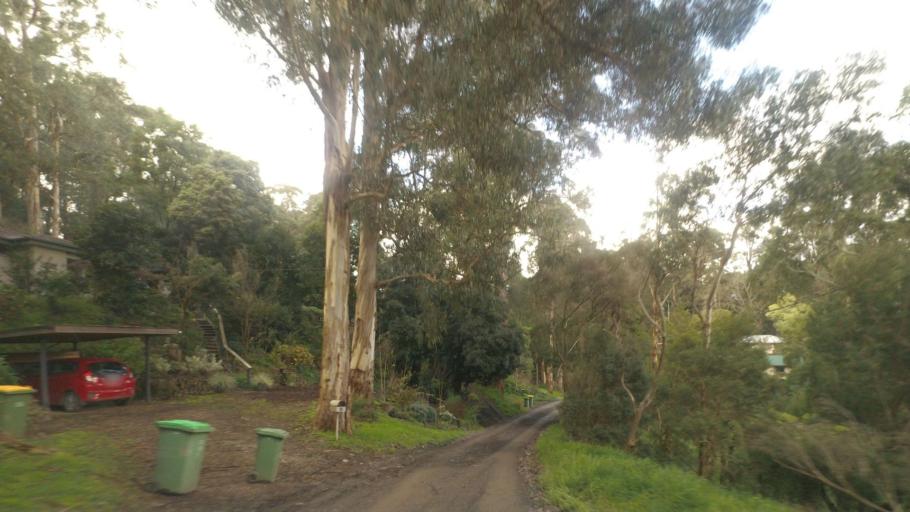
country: AU
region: Victoria
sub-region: Yarra Ranges
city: Selby
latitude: -37.9089
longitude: 145.3690
